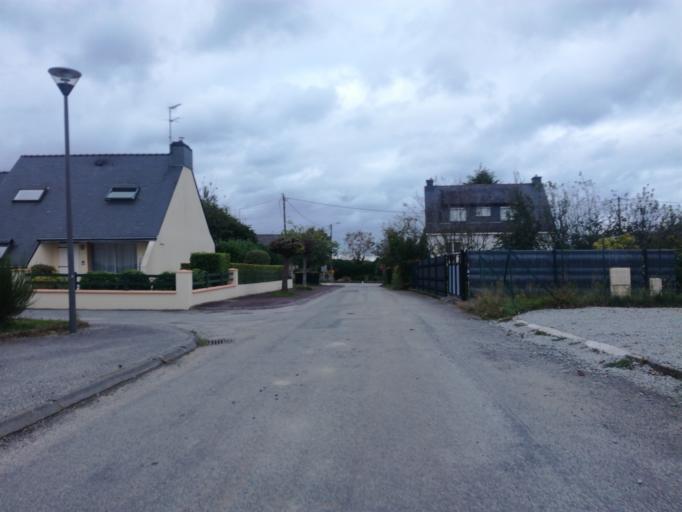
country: FR
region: Brittany
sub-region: Departement du Morbihan
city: Le Sourn
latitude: 48.0410
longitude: -2.9873
